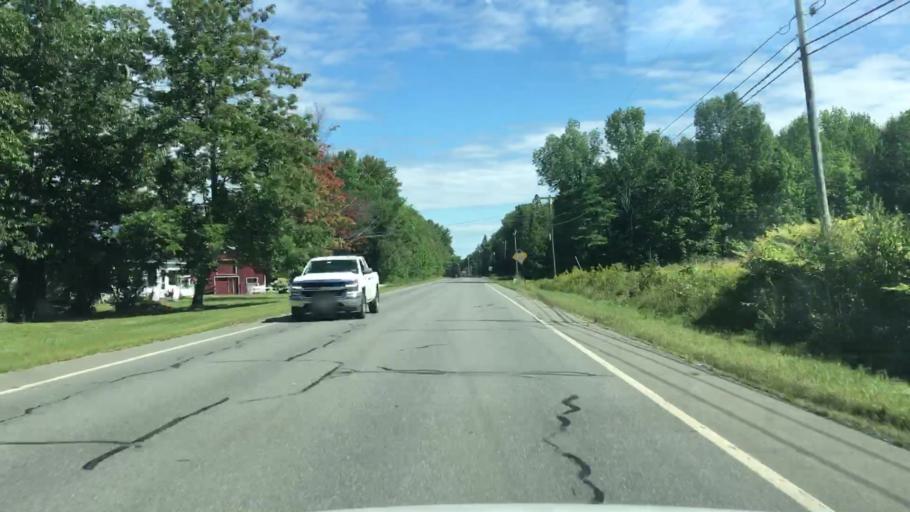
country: US
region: Maine
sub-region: Penobscot County
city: Dexter
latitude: 45.0657
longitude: -69.2432
